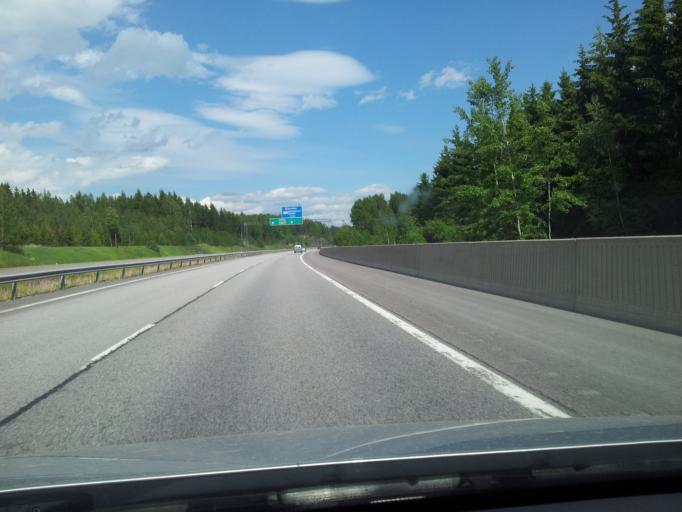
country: FI
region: Uusimaa
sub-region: Loviisa
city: Perna
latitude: 60.4917
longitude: 25.9188
